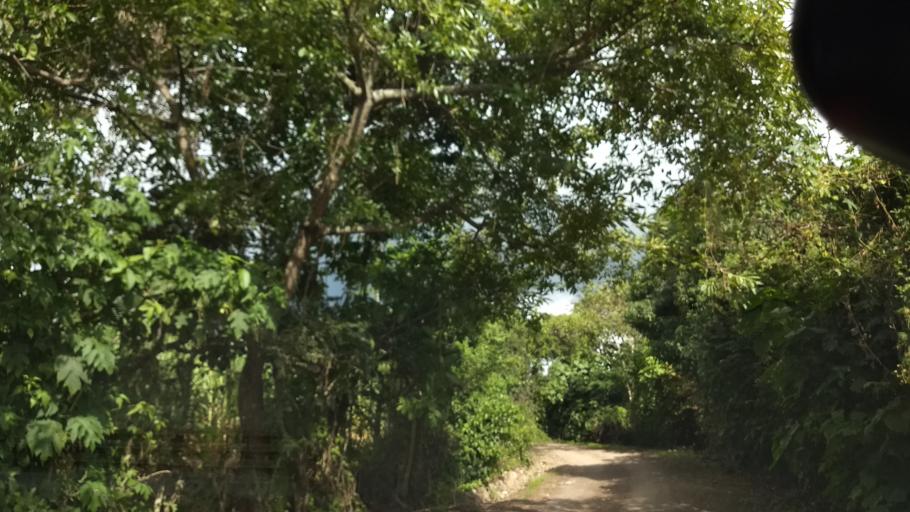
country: MX
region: Colima
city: Suchitlan
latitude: 19.4600
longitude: -103.7625
